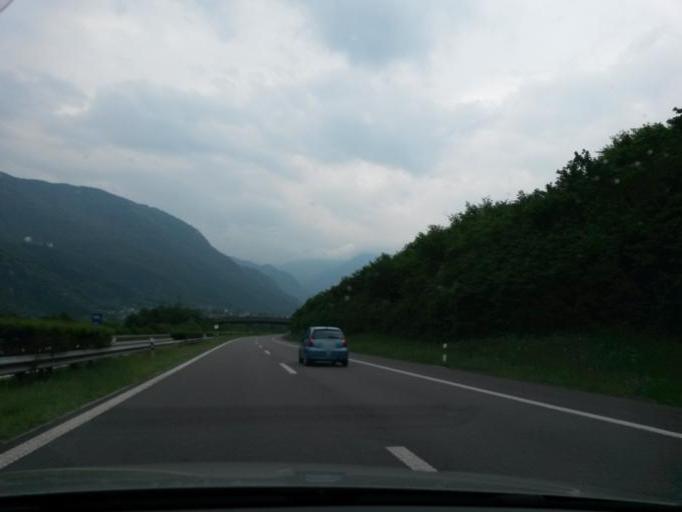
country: CH
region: Ticino
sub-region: Riviera District
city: Claro
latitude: 46.2694
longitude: 9.0033
